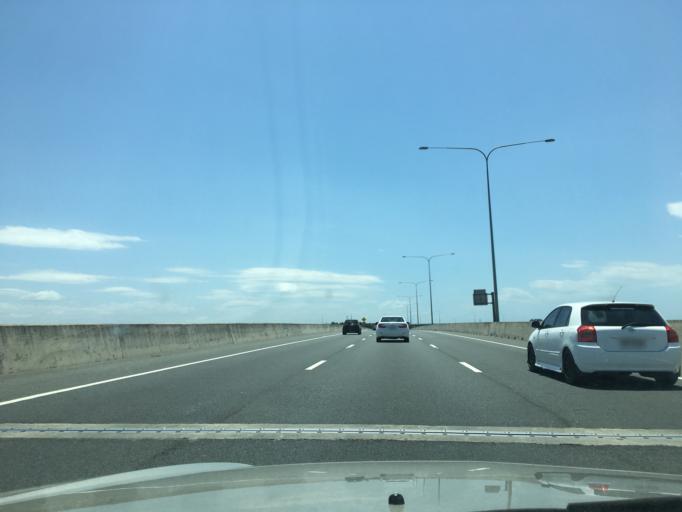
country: AU
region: Queensland
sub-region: Brisbane
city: Wavell Heights
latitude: -27.3976
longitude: 153.0937
